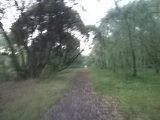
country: RU
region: Moscow
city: Pokrovskoye-Streshnevo
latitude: 55.8169
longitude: 37.4816
